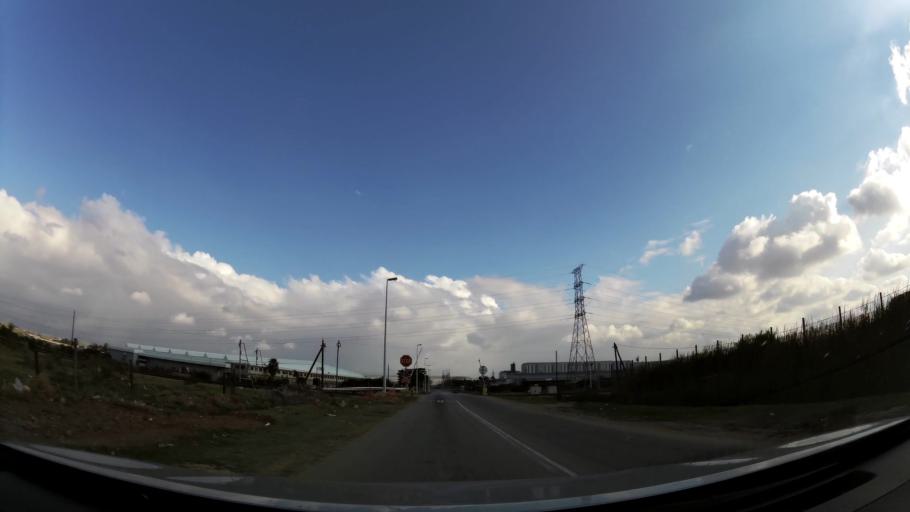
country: ZA
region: Eastern Cape
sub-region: Nelson Mandela Bay Metropolitan Municipality
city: Uitenhage
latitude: -33.7835
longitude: 25.4274
